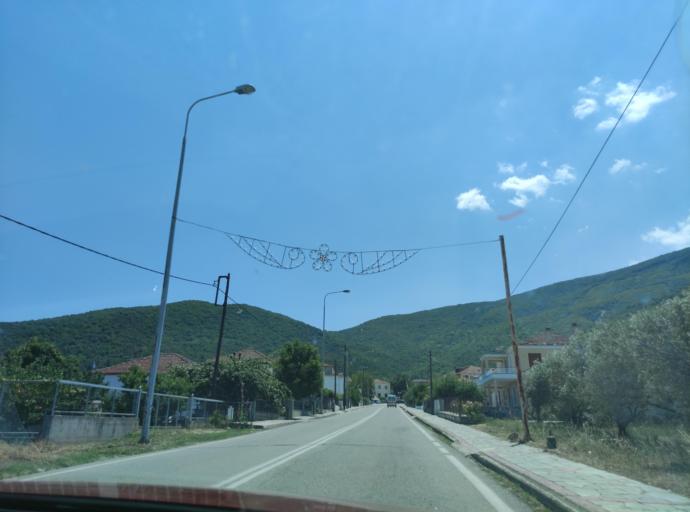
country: GR
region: East Macedonia and Thrace
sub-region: Nomos Kavalas
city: Palaiochori
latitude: 40.9483
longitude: 24.2087
